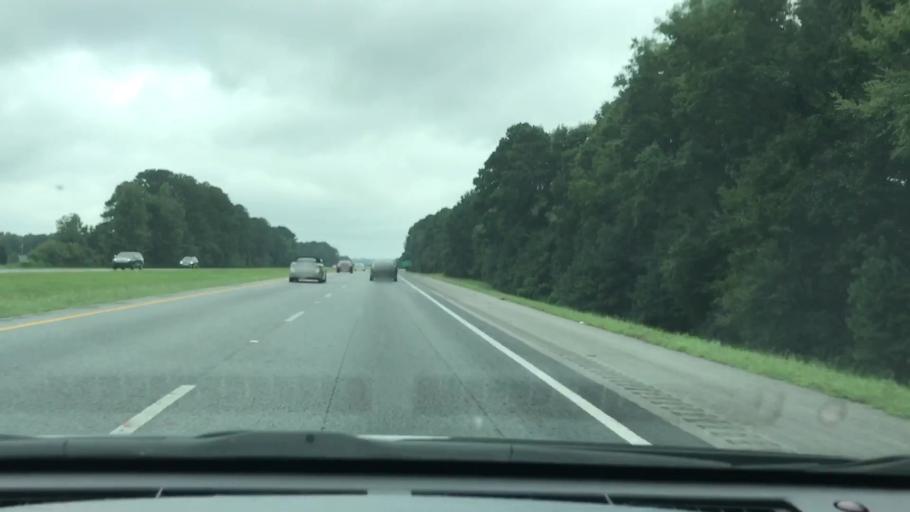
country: US
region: Georgia
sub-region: Walton County
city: Social Circle
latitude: 33.5899
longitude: -83.6199
